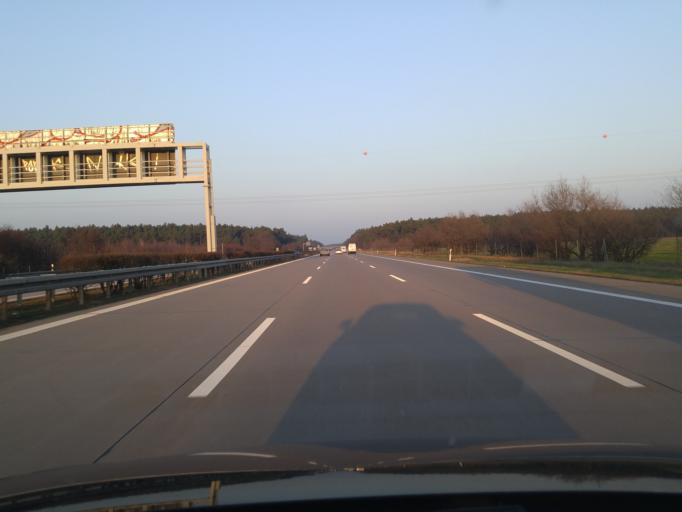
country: DE
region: Brandenburg
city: Wollin
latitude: 52.2962
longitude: 12.4663
